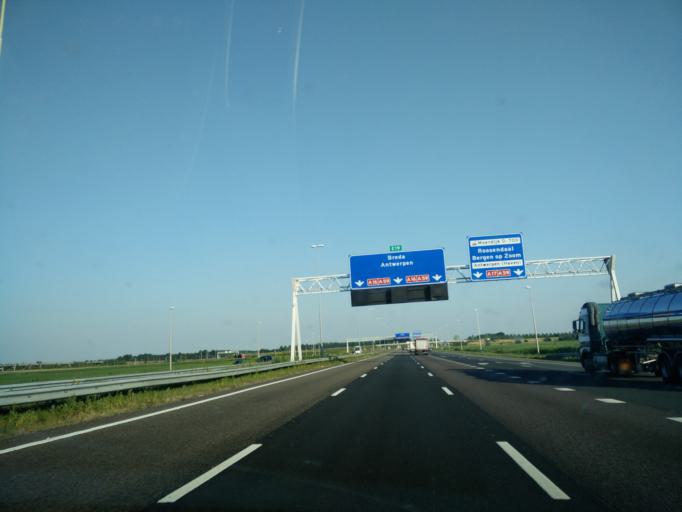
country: NL
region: South Holland
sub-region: Gemeente Strijen
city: Strijen
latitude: 51.7071
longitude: 4.6437
